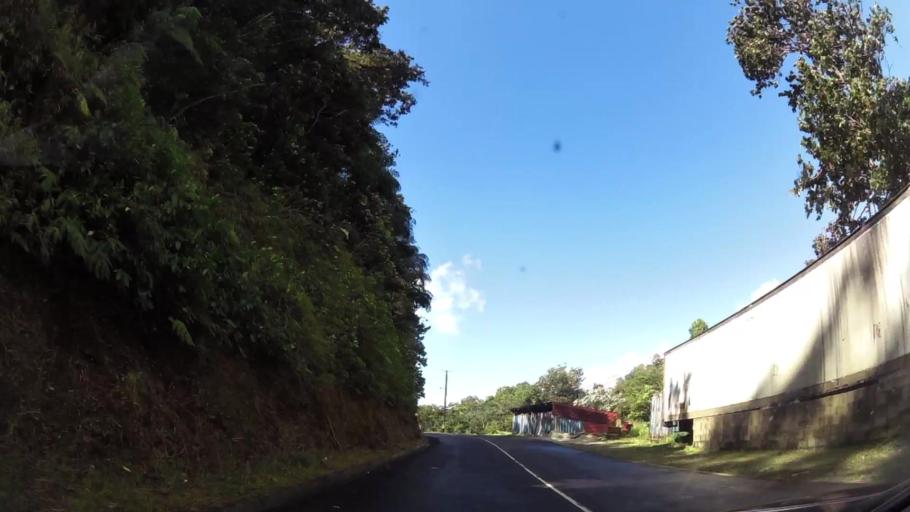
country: DM
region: Saint Paul
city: Pont Casse
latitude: 15.3727
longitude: -61.3464
